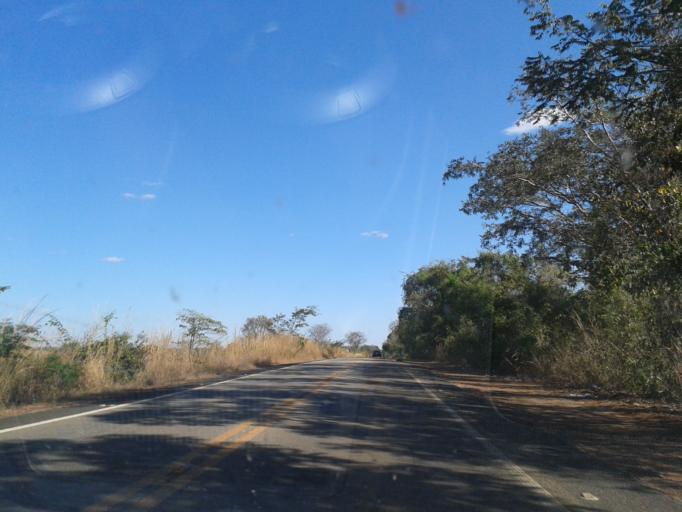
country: BR
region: Goias
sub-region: Mozarlandia
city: Mozarlandia
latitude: -14.6792
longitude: -50.5380
